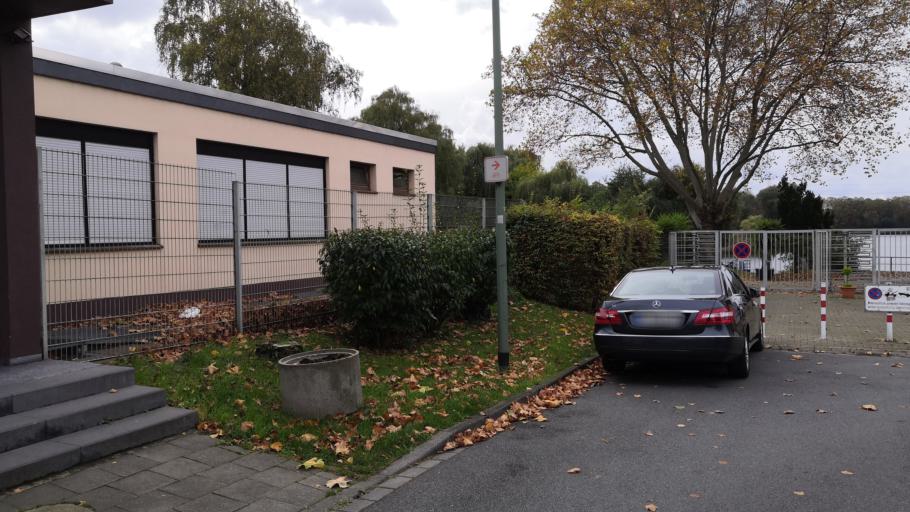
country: DE
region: North Rhine-Westphalia
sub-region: Regierungsbezirk Dusseldorf
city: Hochfeld
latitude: 51.3907
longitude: 6.7036
